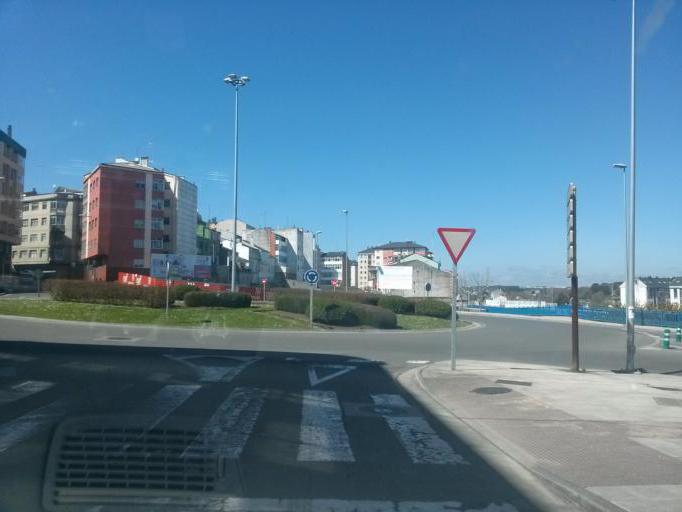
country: ES
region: Galicia
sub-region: Provincia de Lugo
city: Lugo
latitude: 43.0158
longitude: -7.5552
